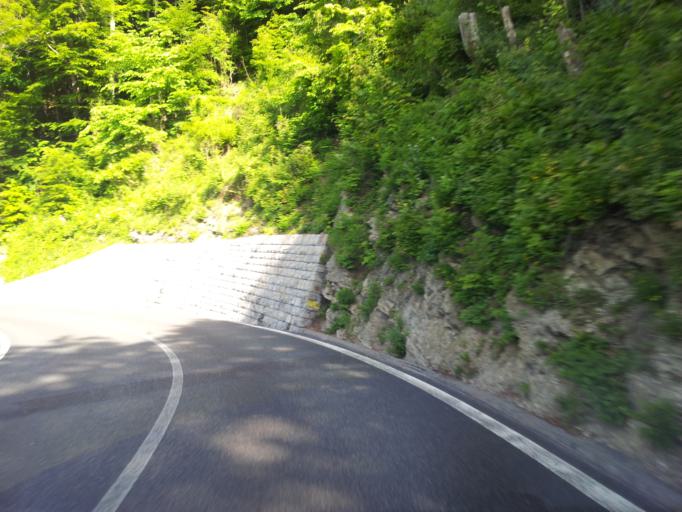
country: CH
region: Obwalden
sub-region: Obwalden
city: Lungern
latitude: 46.7515
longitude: 8.1275
